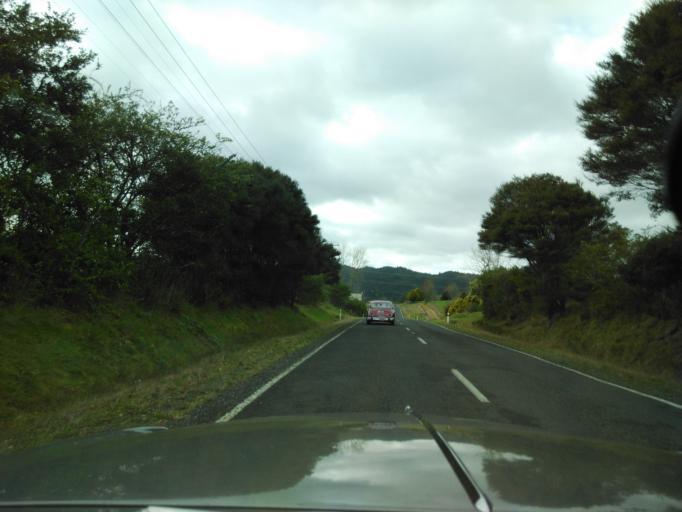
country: NZ
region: Auckland
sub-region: Auckland
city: Red Hill
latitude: -37.1105
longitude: 175.0816
